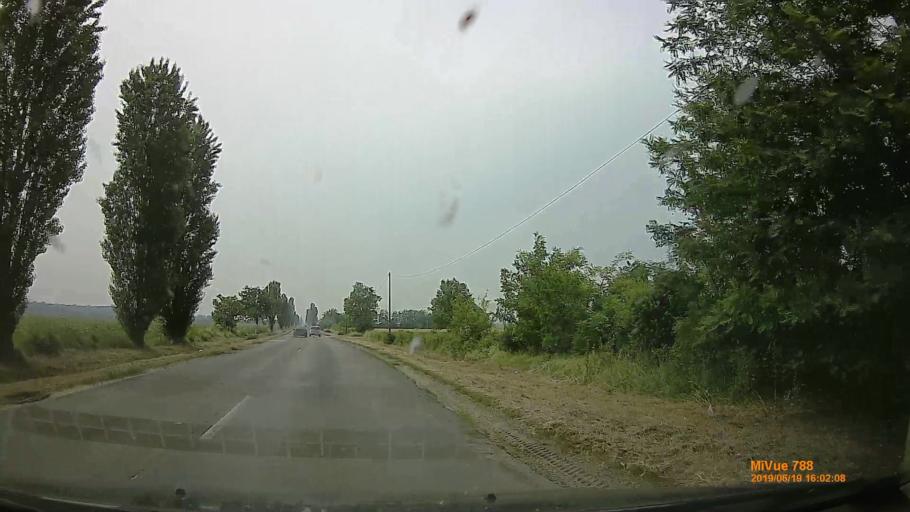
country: HU
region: Baranya
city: Szigetvar
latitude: 46.0557
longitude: 17.7799
